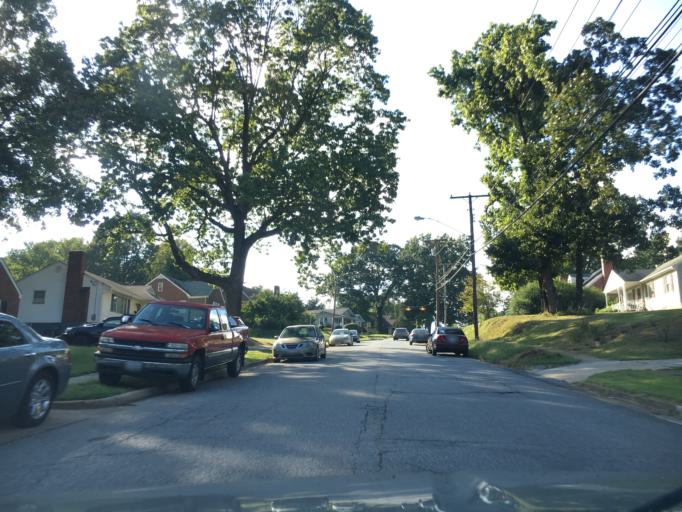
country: US
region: Virginia
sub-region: City of Lynchburg
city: West Lynchburg
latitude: 37.3858
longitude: -79.1820
